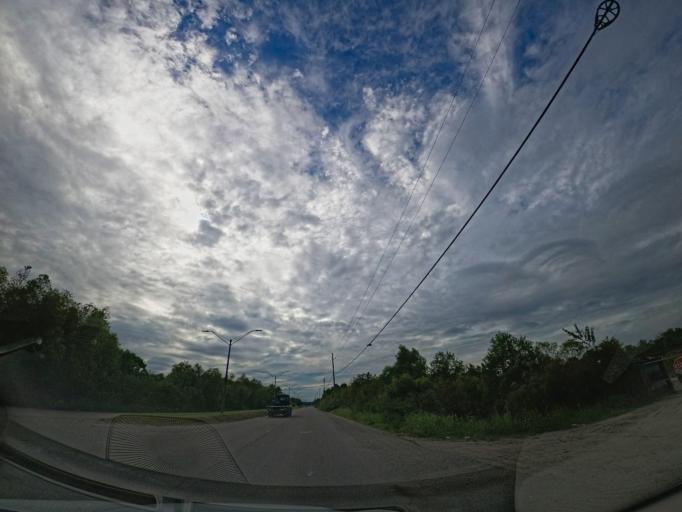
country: US
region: Louisiana
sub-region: Saint Bernard Parish
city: Arabi
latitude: 30.0092
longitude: -89.9852
